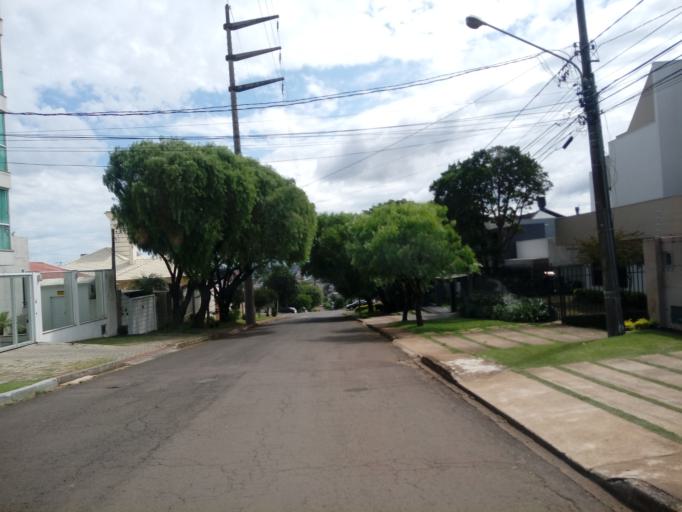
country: BR
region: Santa Catarina
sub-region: Chapeco
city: Chapeco
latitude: -27.1026
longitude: -52.6008
